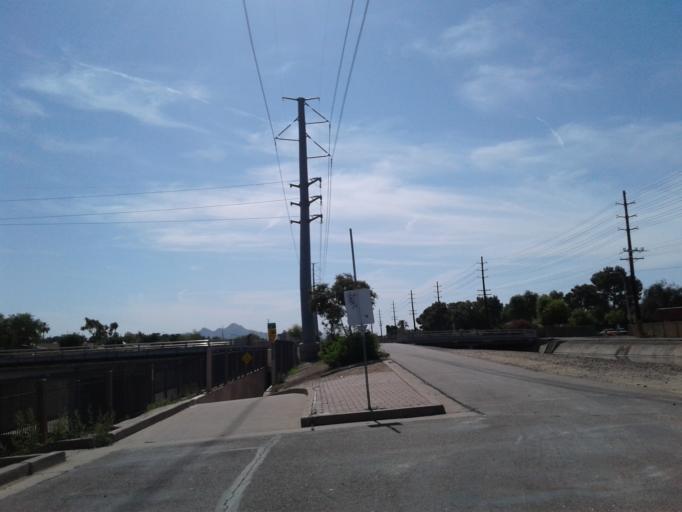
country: US
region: Arizona
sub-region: Maricopa County
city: Glendale
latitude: 33.5726
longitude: -112.1352
